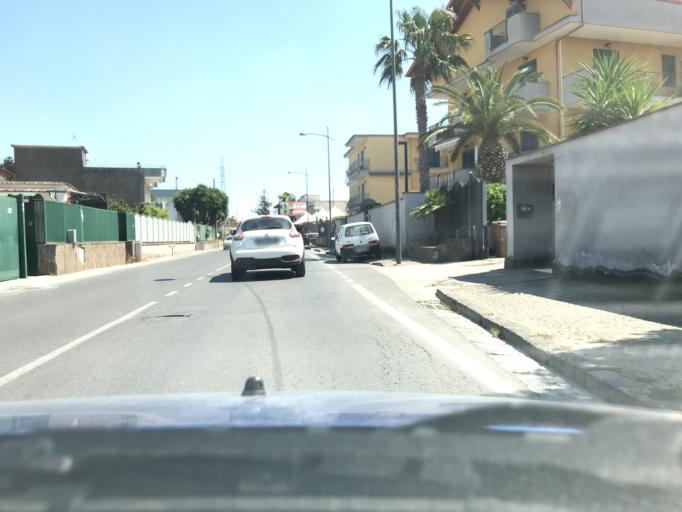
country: IT
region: Campania
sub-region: Provincia di Napoli
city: Villaricca
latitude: 40.9185
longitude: 14.1789
